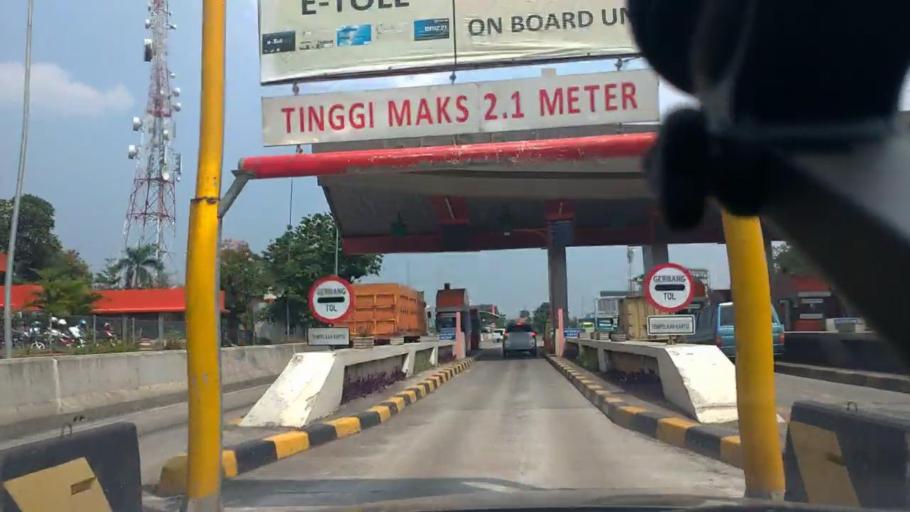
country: ID
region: Banten
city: Serang
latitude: -6.1160
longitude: 106.1833
